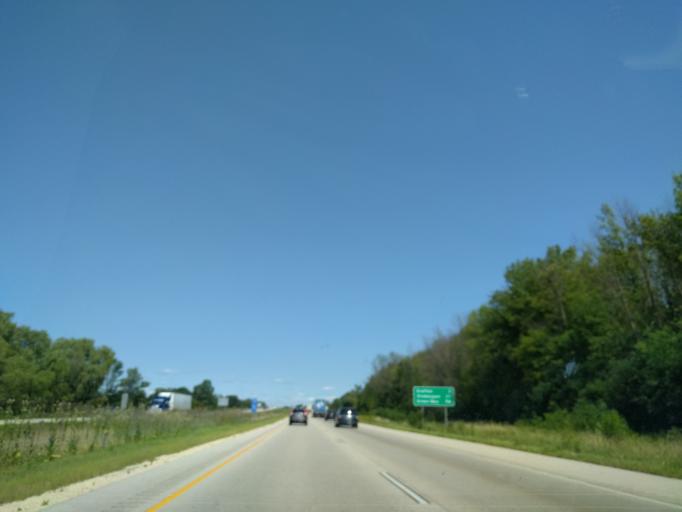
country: US
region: Wisconsin
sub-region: Ozaukee County
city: Grafton
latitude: 43.2897
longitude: -87.9207
